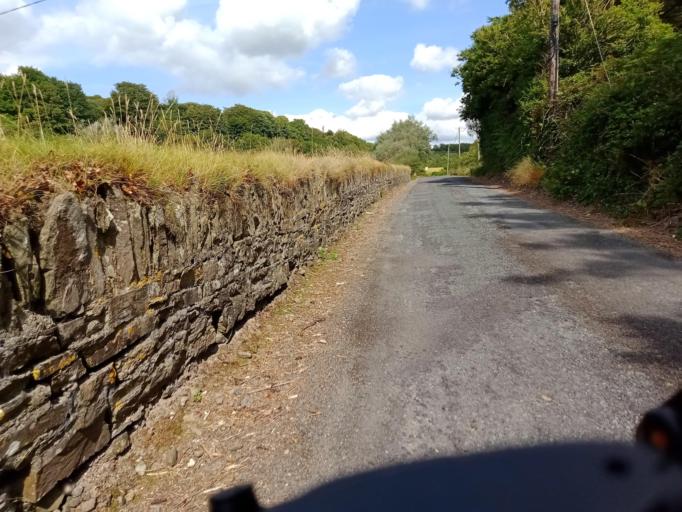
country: IE
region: Munster
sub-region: Waterford
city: Dungarvan
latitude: 52.1070
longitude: -7.5105
